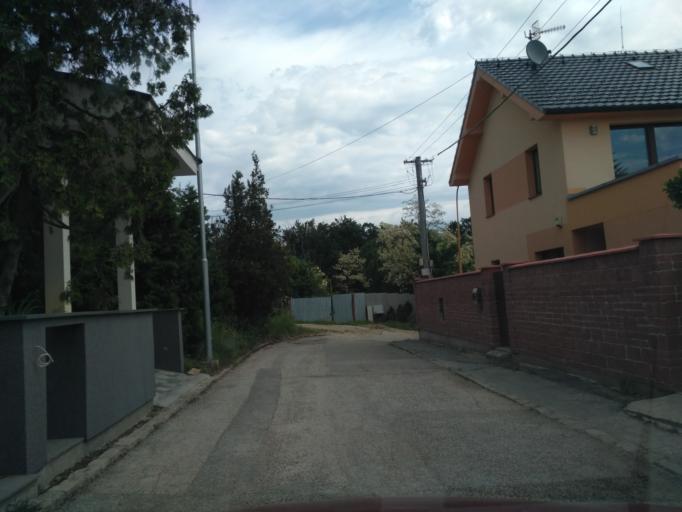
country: SK
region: Kosicky
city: Kosice
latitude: 48.7327
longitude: 21.2317
